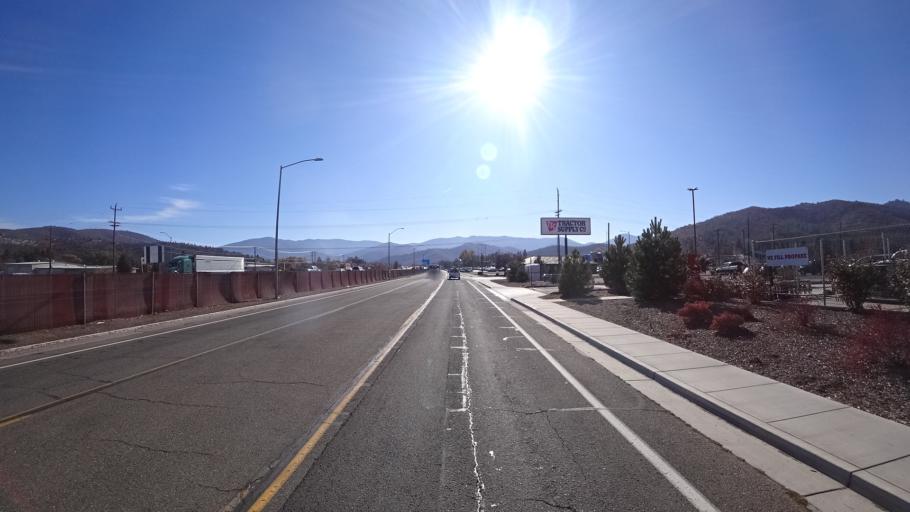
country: US
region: California
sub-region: Siskiyou County
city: Yreka
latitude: 41.7129
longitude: -122.6417
